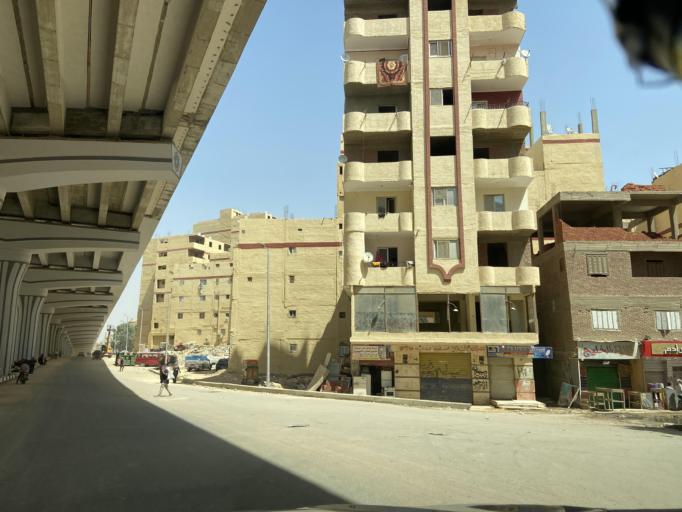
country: EG
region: Muhafazat al Qahirah
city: Cairo
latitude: 30.0640
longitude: 31.3813
